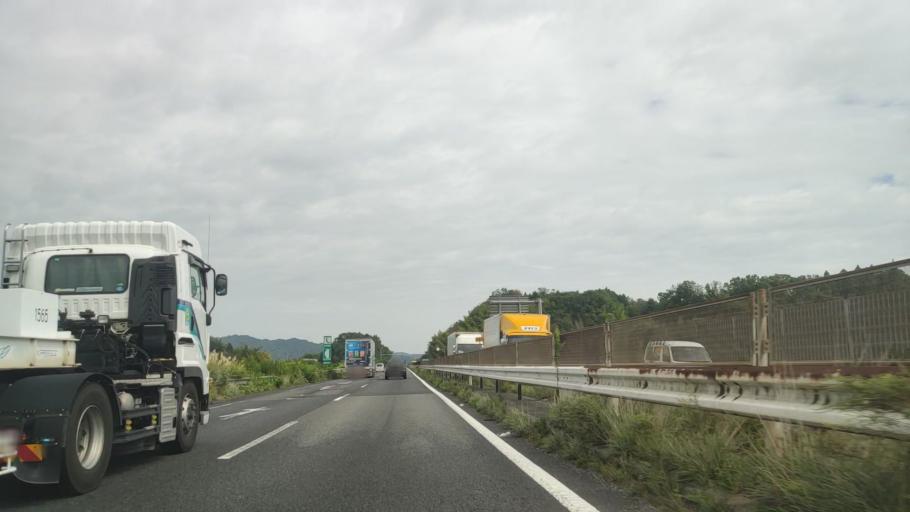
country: JP
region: Mie
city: Ueno-ebisumachi
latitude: 34.7815
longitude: 136.1586
